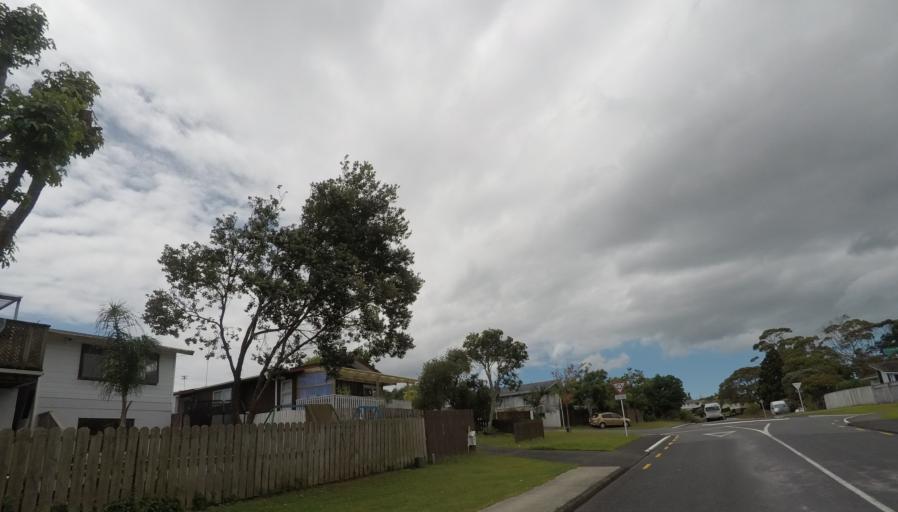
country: NZ
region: Auckland
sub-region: Auckland
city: Rosebank
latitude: -36.8487
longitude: 174.6108
